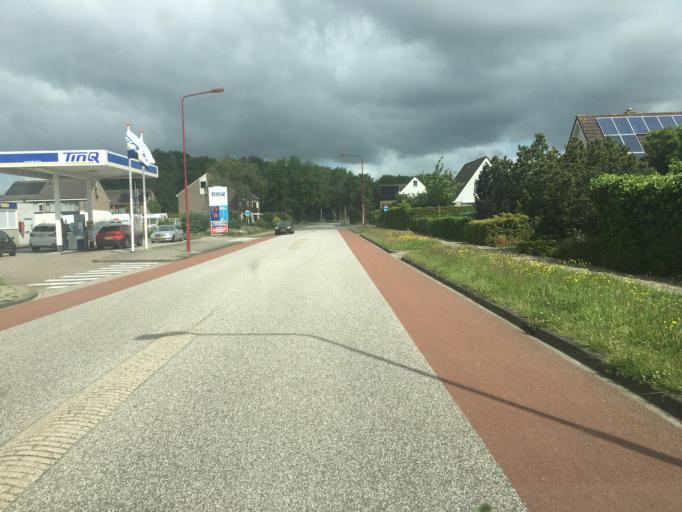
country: NL
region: Friesland
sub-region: Gemeente Heerenveen
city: Heerenveen
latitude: 52.9449
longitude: 5.9188
